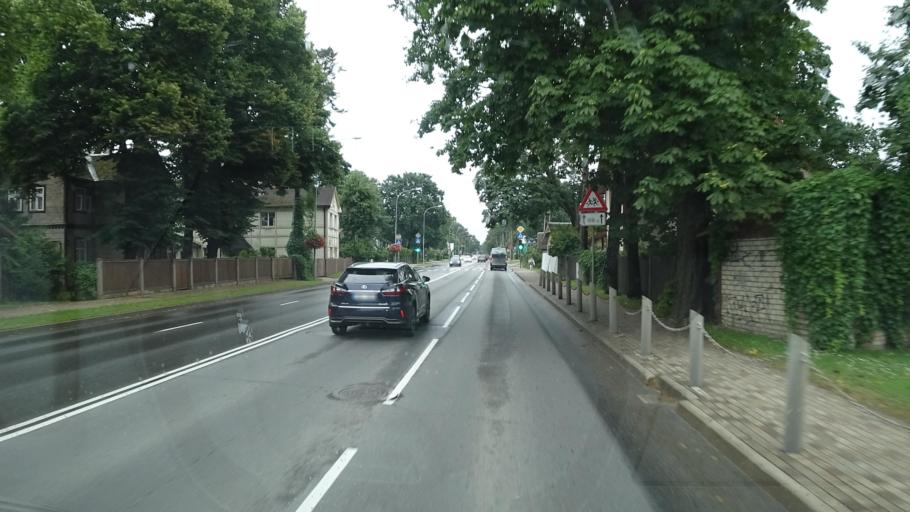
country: LV
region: Jurmala
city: Jurmala
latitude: 56.9698
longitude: 23.8019
